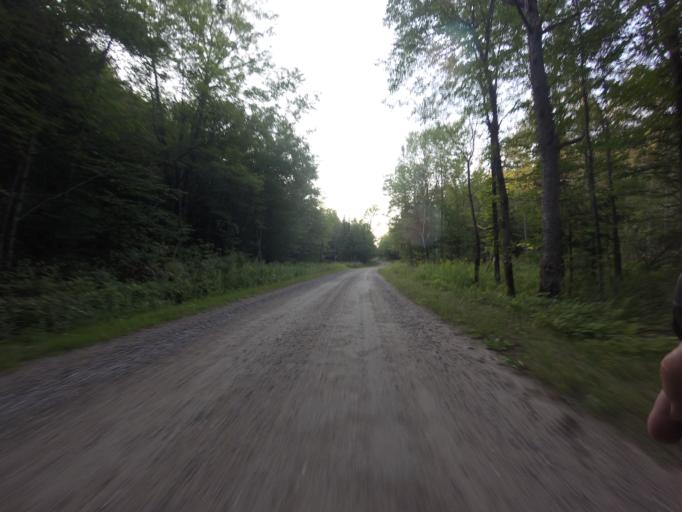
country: CA
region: Ontario
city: Renfrew
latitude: 45.0476
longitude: -76.7466
